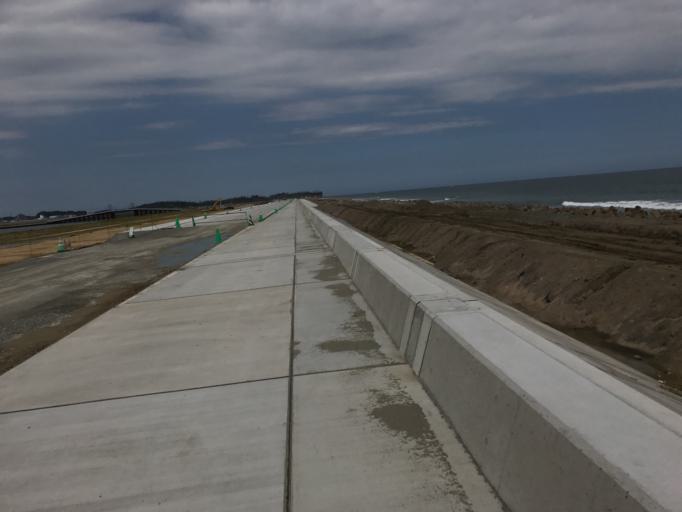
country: JP
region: Miyagi
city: Marumori
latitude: 37.7988
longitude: 140.9859
